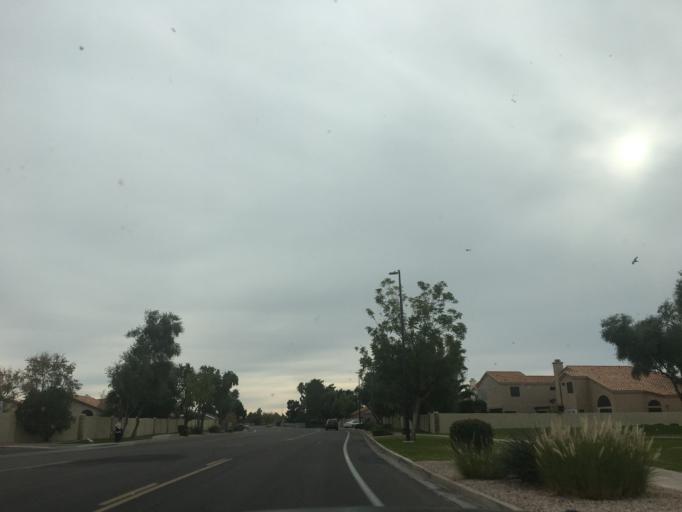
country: US
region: Arizona
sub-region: Maricopa County
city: Gilbert
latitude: 33.3551
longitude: -111.7817
